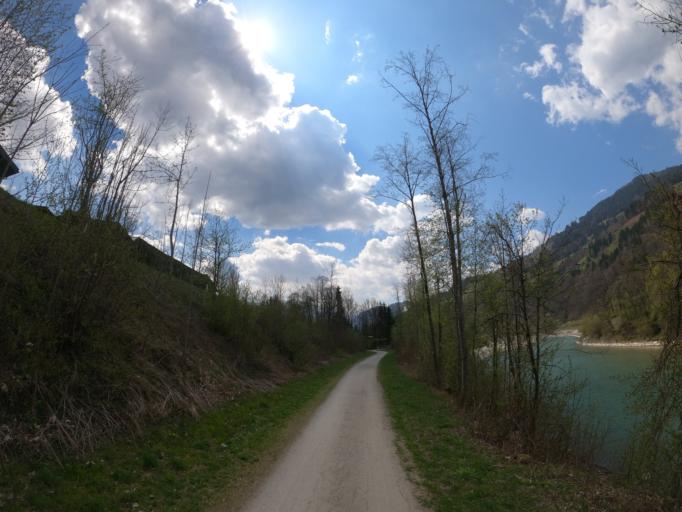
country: AT
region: Salzburg
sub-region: Politischer Bezirk Sankt Johann im Pongau
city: Sankt Johann im Pongau
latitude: 47.3778
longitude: 13.2145
